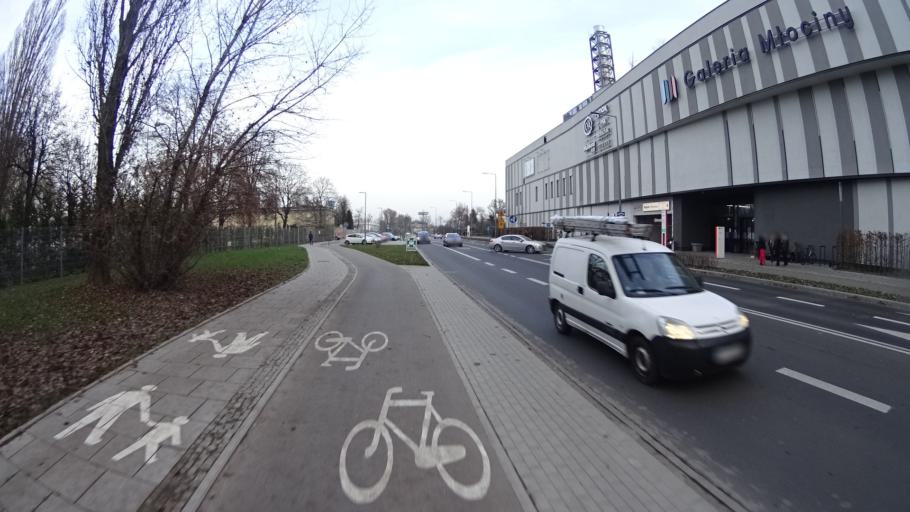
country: PL
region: Masovian Voivodeship
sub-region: Warszawa
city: Bielany
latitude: 52.2963
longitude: 20.9307
